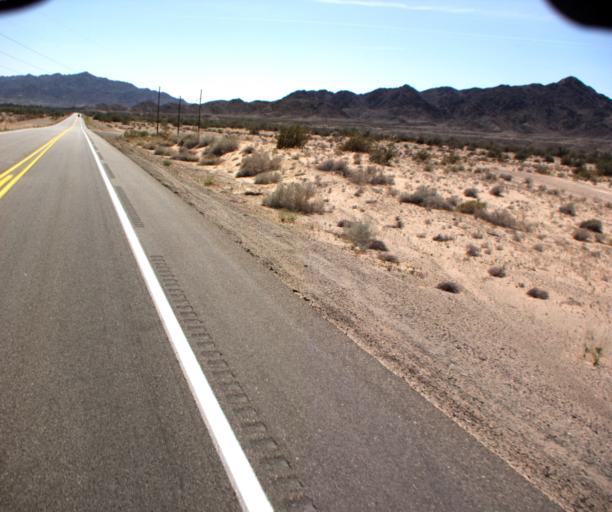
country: US
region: Arizona
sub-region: Yuma County
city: Fortuna Foothills
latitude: 32.8065
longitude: -114.3802
